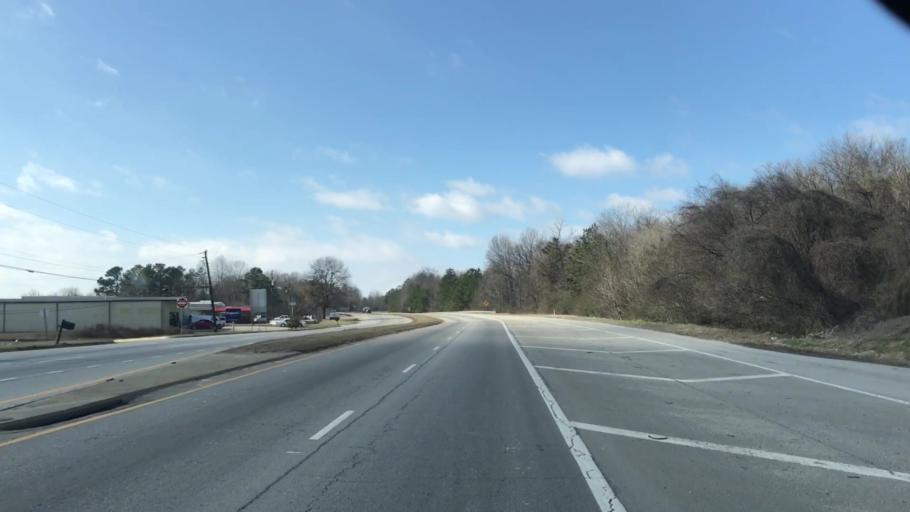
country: US
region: Georgia
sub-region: Hall County
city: Gainesville
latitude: 34.2818
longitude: -83.7913
